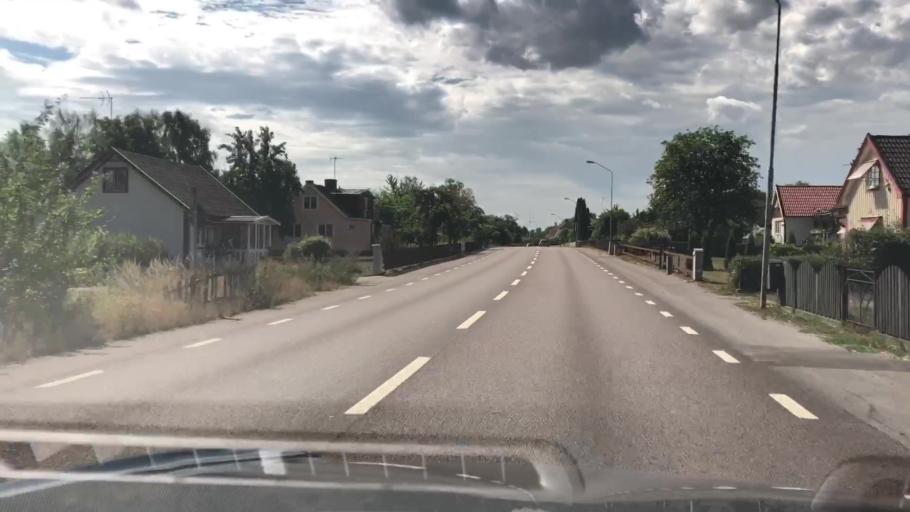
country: SE
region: Kalmar
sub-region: Torsas Kommun
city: Torsas
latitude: 56.3995
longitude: 16.0681
